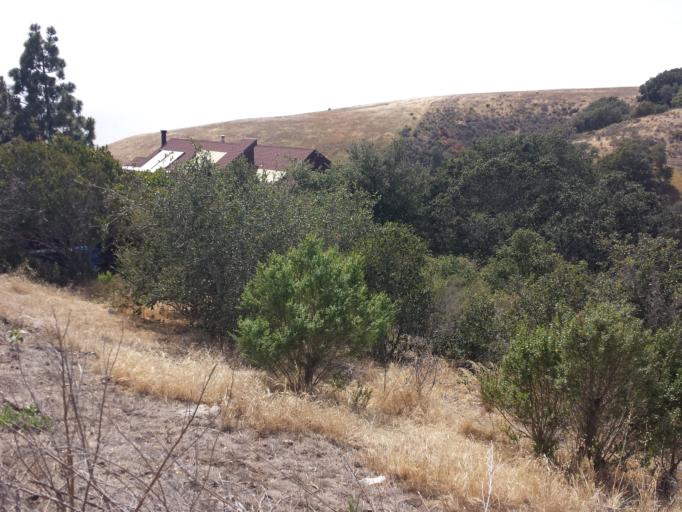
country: US
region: California
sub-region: San Luis Obispo County
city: Pismo Beach
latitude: 35.1509
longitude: -120.6398
